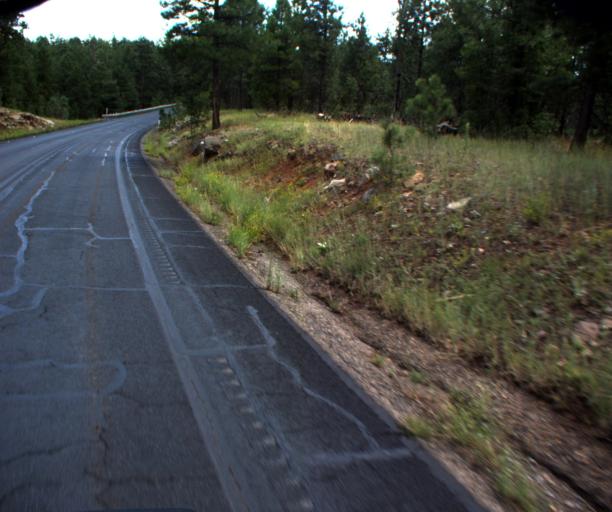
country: US
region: Arizona
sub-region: Gila County
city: Pine
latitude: 34.5004
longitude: -111.4624
